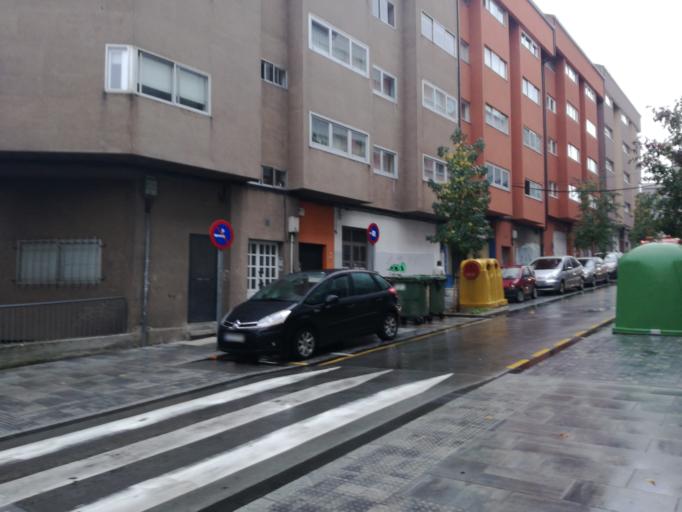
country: ES
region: Galicia
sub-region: Provincia da Coruna
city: Santiago de Compostela
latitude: 42.8781
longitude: -8.5354
